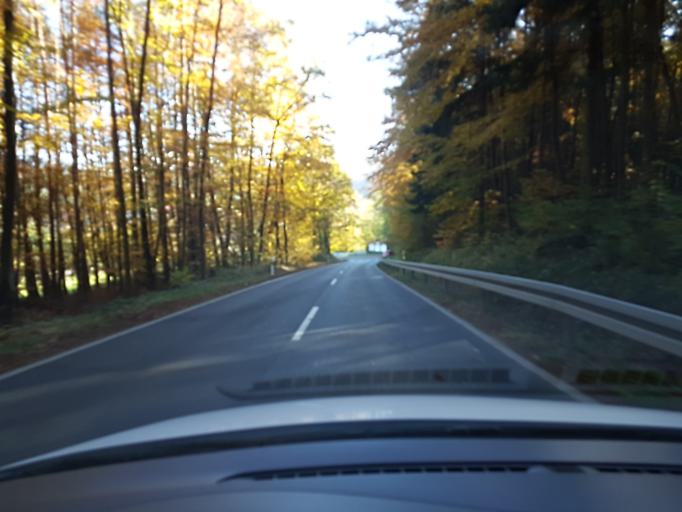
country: DE
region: Bavaria
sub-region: Regierungsbezirk Unterfranken
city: Leidersbach
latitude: 49.8776
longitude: 9.2403
